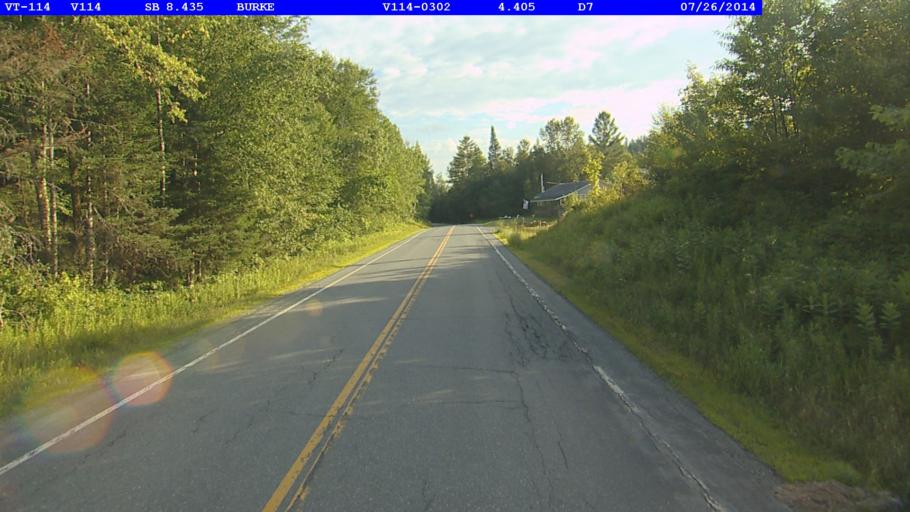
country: US
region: Vermont
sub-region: Caledonia County
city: Lyndonville
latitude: 44.6312
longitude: -71.8994
